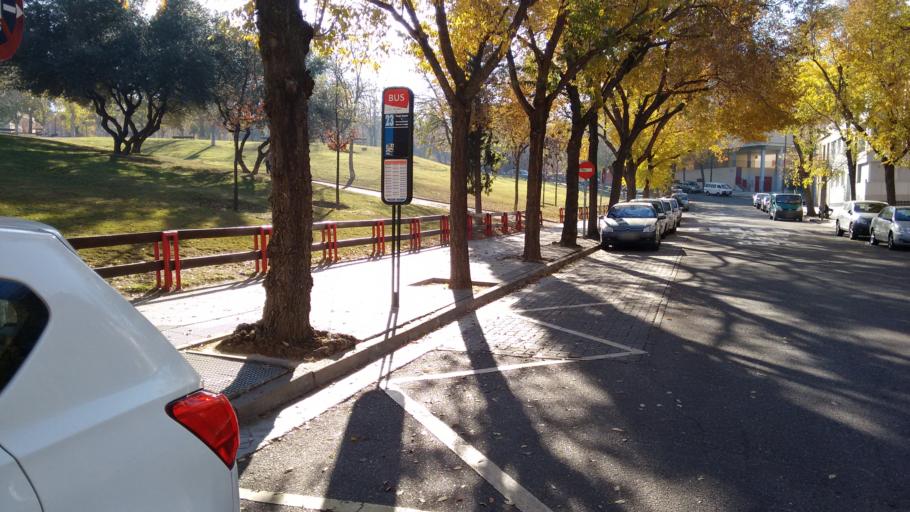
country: ES
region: Aragon
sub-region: Provincia de Zaragoza
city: Zaragoza
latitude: 41.6295
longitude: -0.8799
